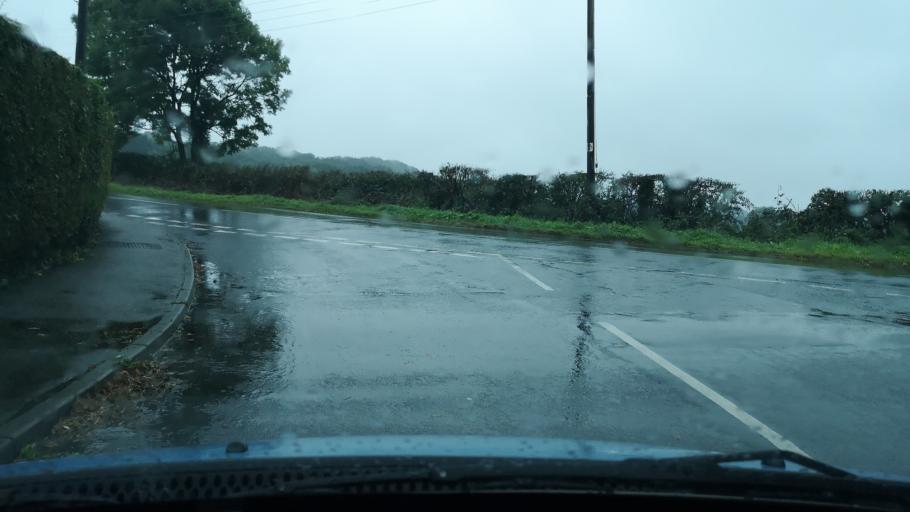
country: GB
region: England
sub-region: City and Borough of Wakefield
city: Sharlston
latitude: 53.6624
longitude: -1.4122
